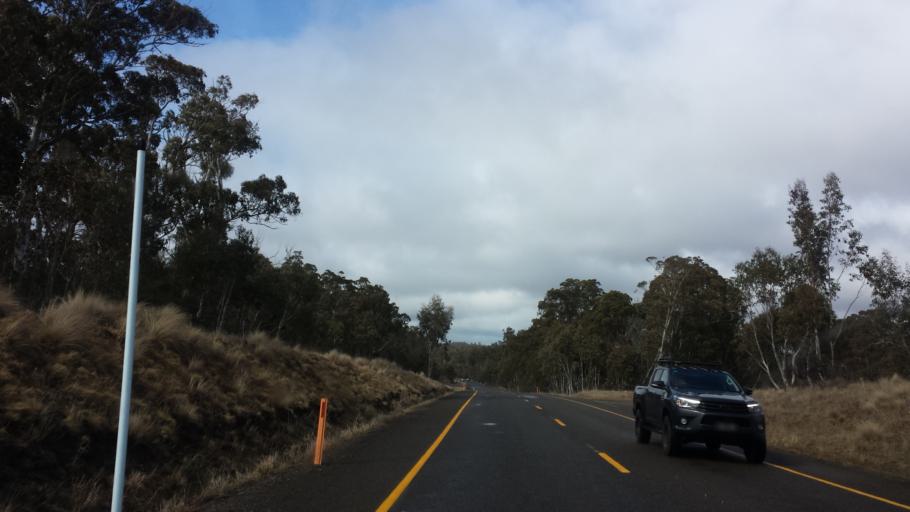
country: AU
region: Victoria
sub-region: Alpine
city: Mount Beauty
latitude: -37.0641
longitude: 147.3377
